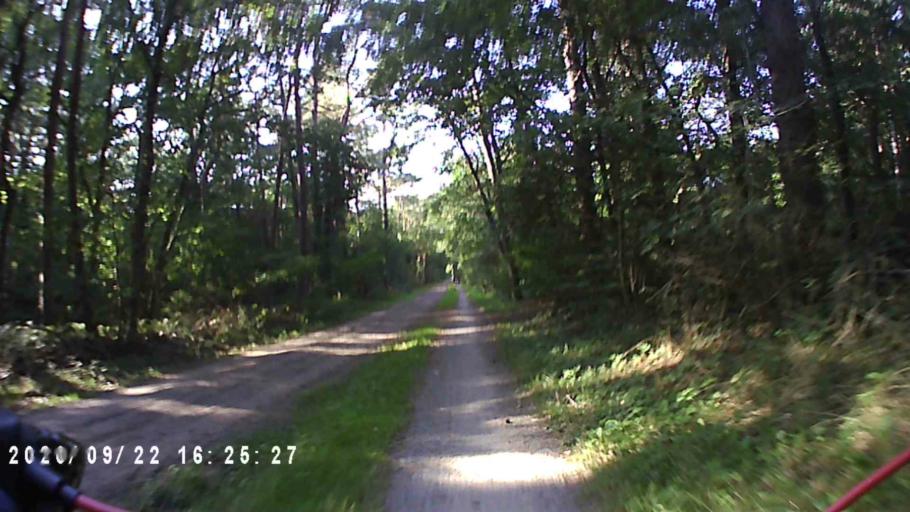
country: NL
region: Groningen
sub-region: Gemeente Leek
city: Leek
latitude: 53.0762
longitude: 6.4387
